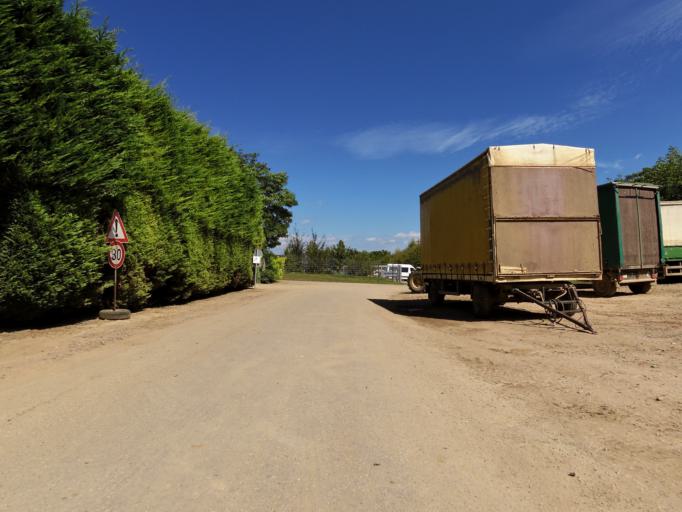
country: DE
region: Rheinland-Pfalz
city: Weingarten
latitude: 49.2627
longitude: 8.2910
